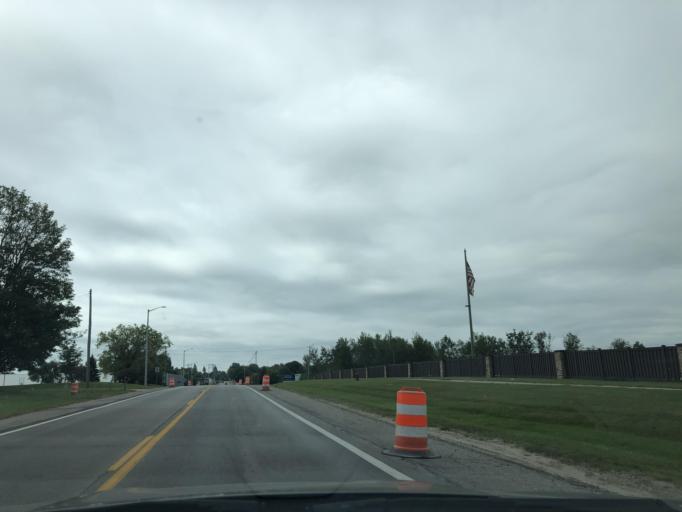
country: US
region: Michigan
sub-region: Missaukee County
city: Lake City
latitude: 44.1995
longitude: -85.2140
